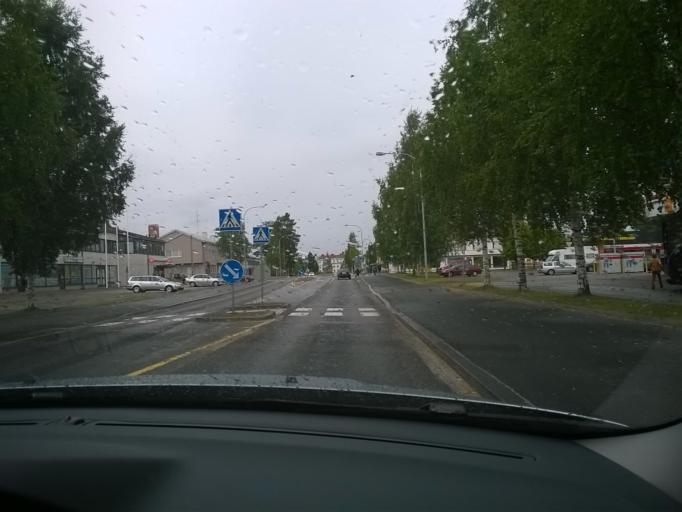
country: FI
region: Kainuu
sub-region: Kehys-Kainuu
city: Kuhmo
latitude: 64.1269
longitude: 29.5252
